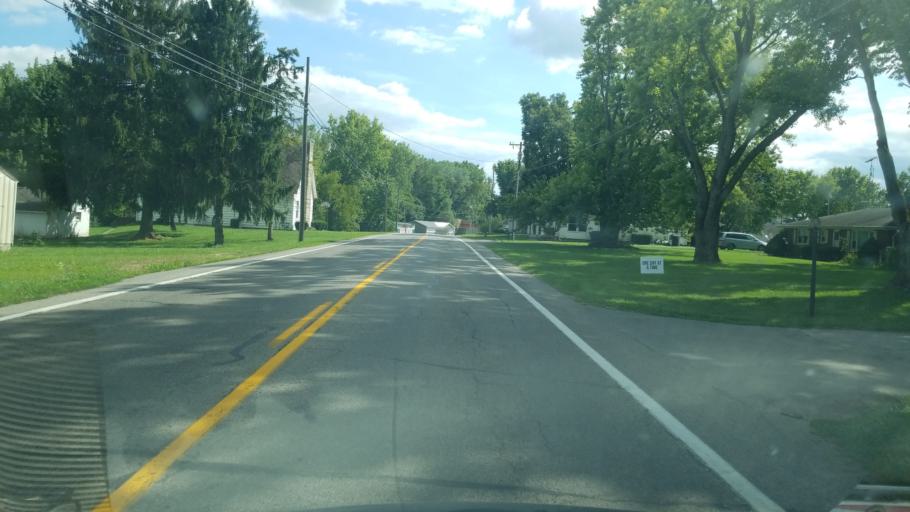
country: US
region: Ohio
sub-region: Logan County
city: De Graff
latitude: 40.3163
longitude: -83.9124
